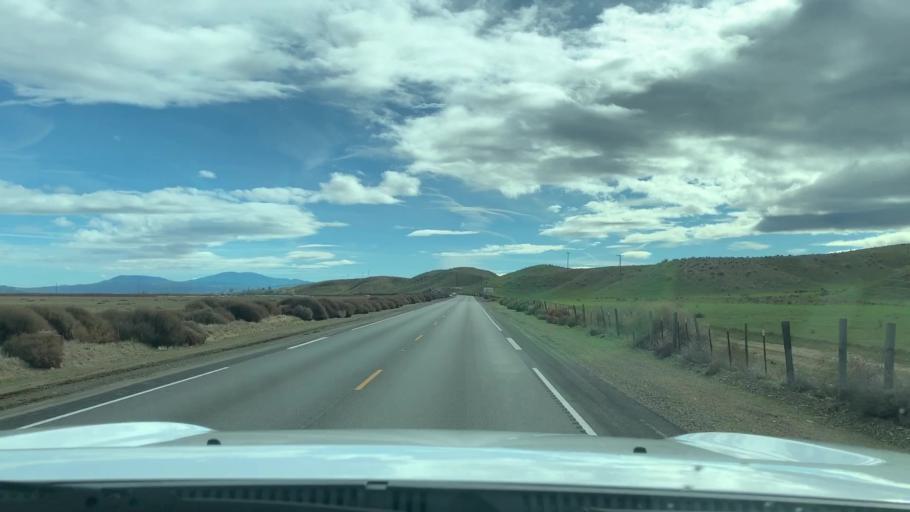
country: US
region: California
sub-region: Kern County
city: Taft Heights
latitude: 34.9695
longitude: -119.7435
